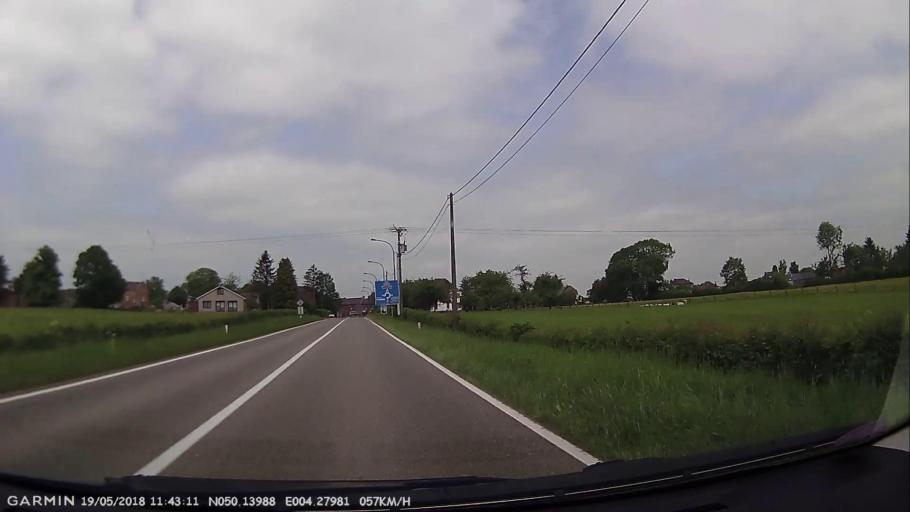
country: BE
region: Wallonia
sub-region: Province du Hainaut
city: Froidchapelle
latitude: 50.1400
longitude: 4.2797
